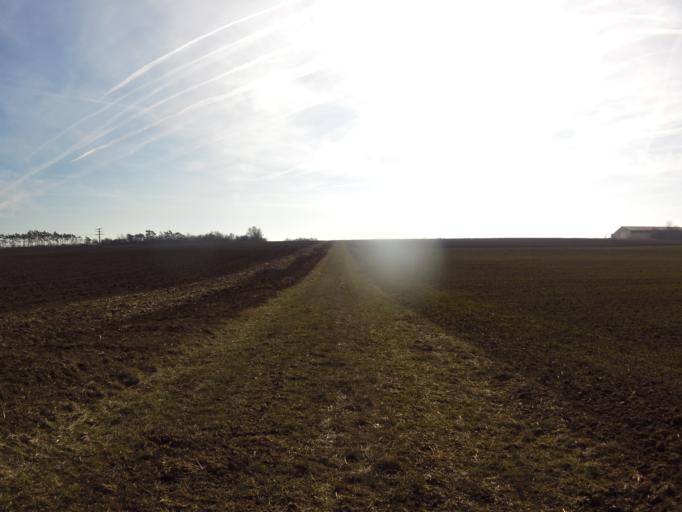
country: DE
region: Bavaria
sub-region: Regierungsbezirk Unterfranken
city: Estenfeld
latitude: 49.8278
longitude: 10.0280
